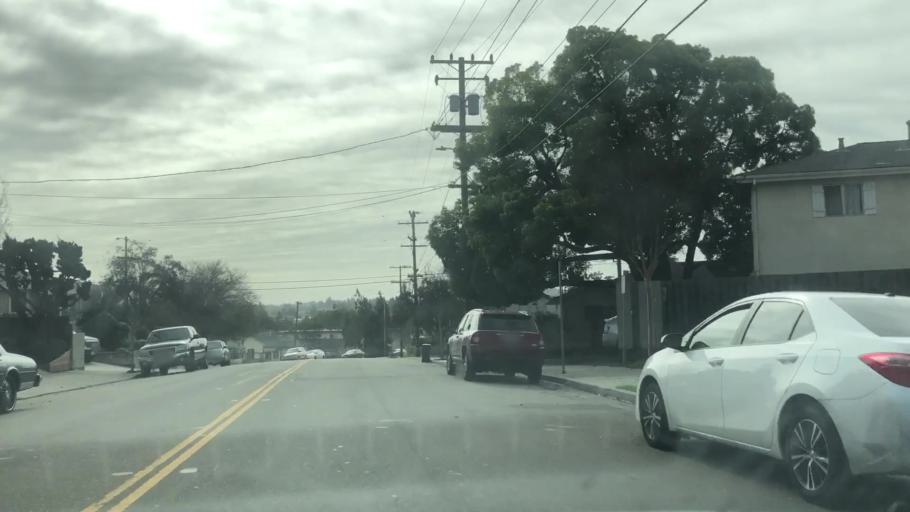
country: US
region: California
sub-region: Alameda County
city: Ashland
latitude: 37.7046
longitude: -122.1170
